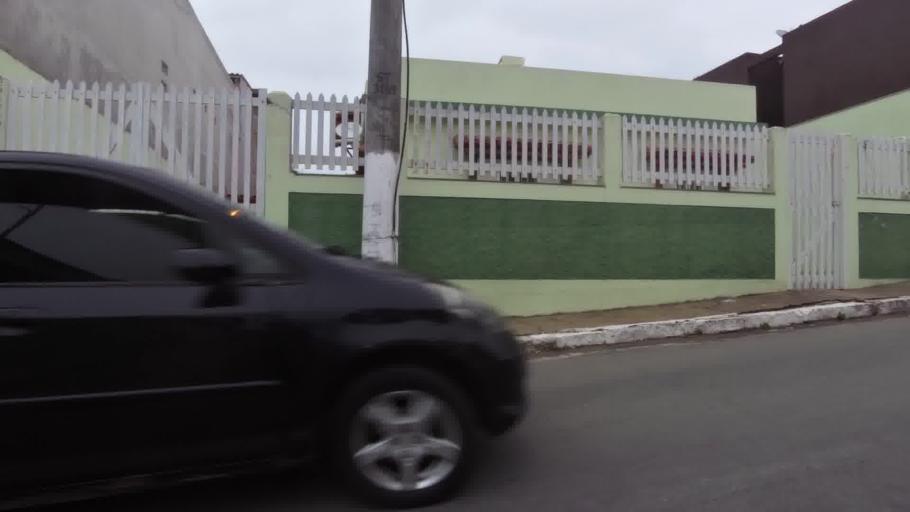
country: BR
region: Espirito Santo
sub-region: Marataizes
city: Marataizes
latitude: -21.0449
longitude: -40.8332
